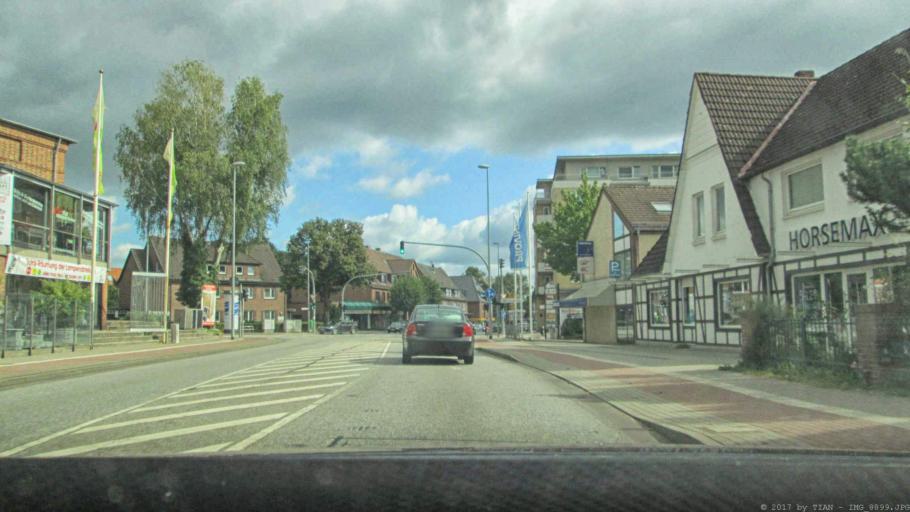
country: DE
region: Schleswig-Holstein
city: Norderstedt
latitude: 53.6814
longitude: 9.9957
